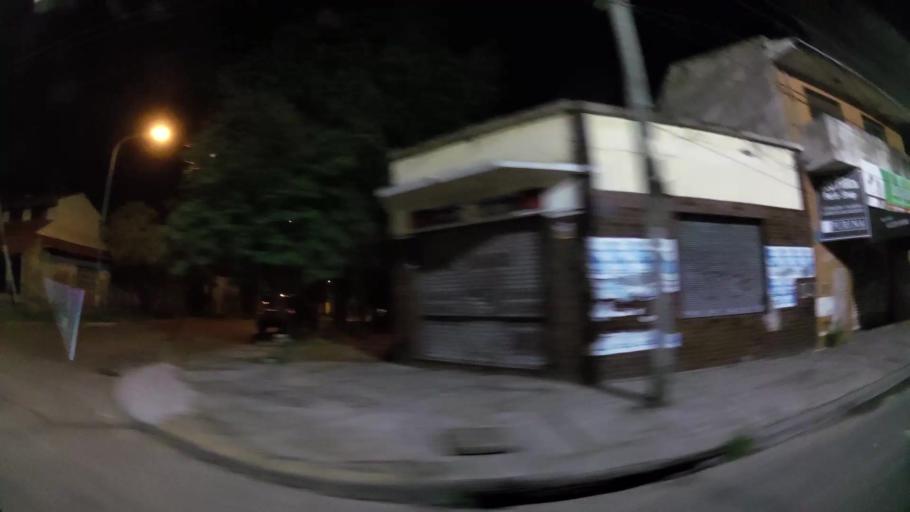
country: AR
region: Buenos Aires
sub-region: Partido de Lanus
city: Lanus
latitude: -34.7140
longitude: -58.3532
